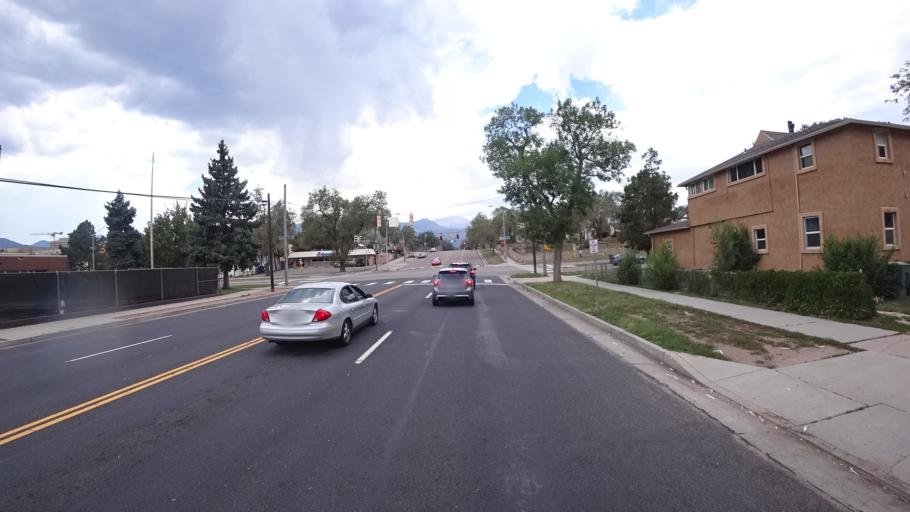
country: US
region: Colorado
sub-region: El Paso County
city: Colorado Springs
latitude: 38.8395
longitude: -104.8170
